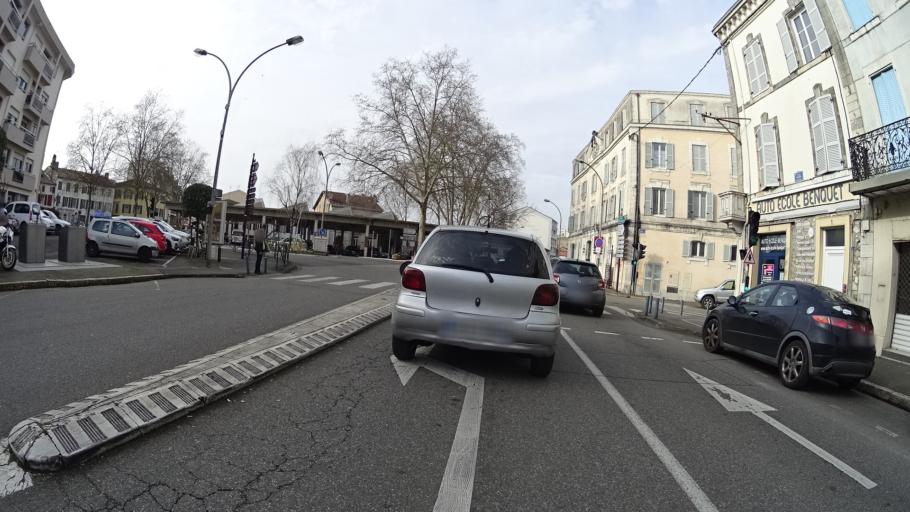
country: FR
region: Aquitaine
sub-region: Departement des Landes
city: Dax
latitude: 43.7083
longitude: -1.0550
